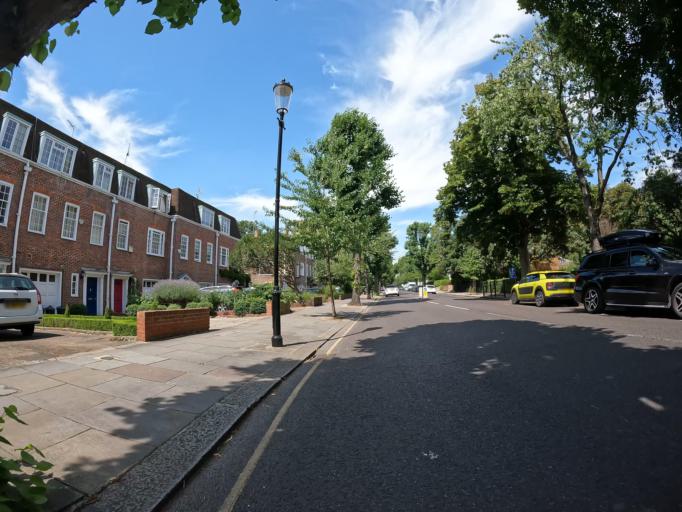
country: GB
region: England
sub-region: Greater London
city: Kensington
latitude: 51.5033
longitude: -0.2077
